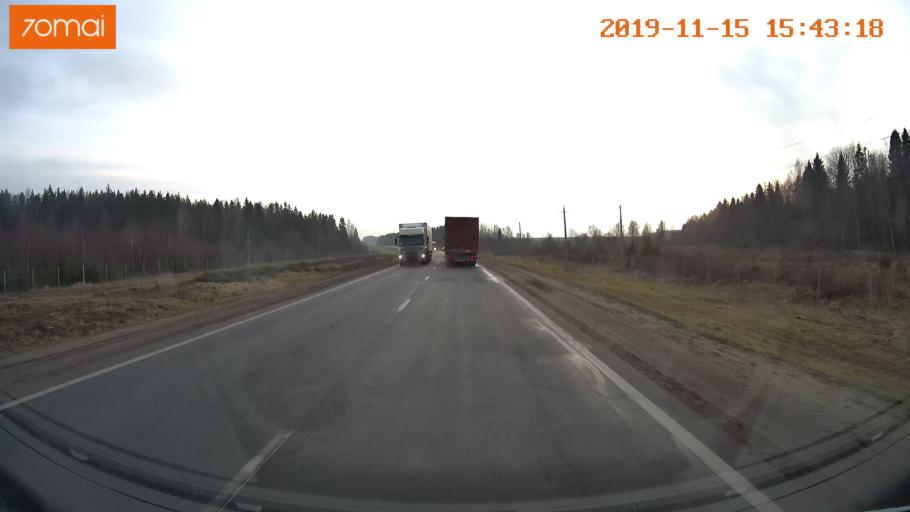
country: RU
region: Jaroslavl
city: Danilov
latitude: 57.9839
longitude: 40.0293
